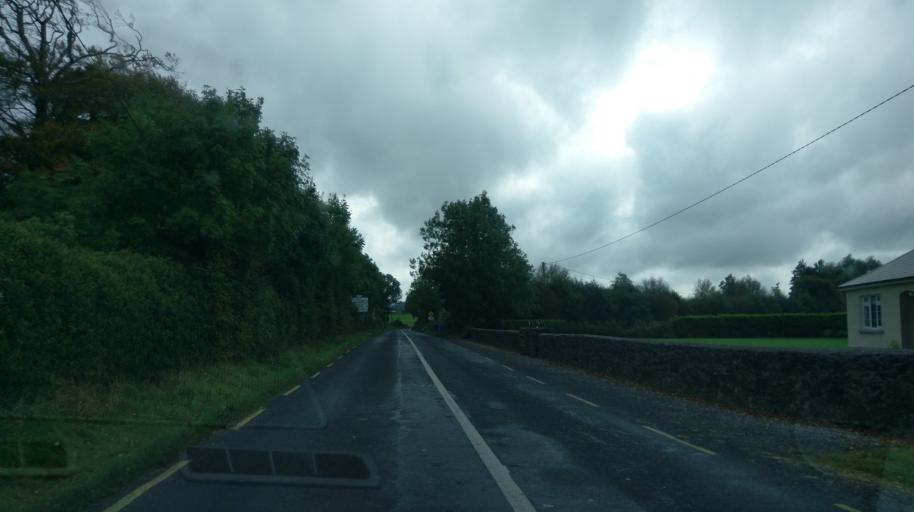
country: IE
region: Connaught
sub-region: County Galway
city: Loughrea
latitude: 53.4471
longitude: -8.4684
